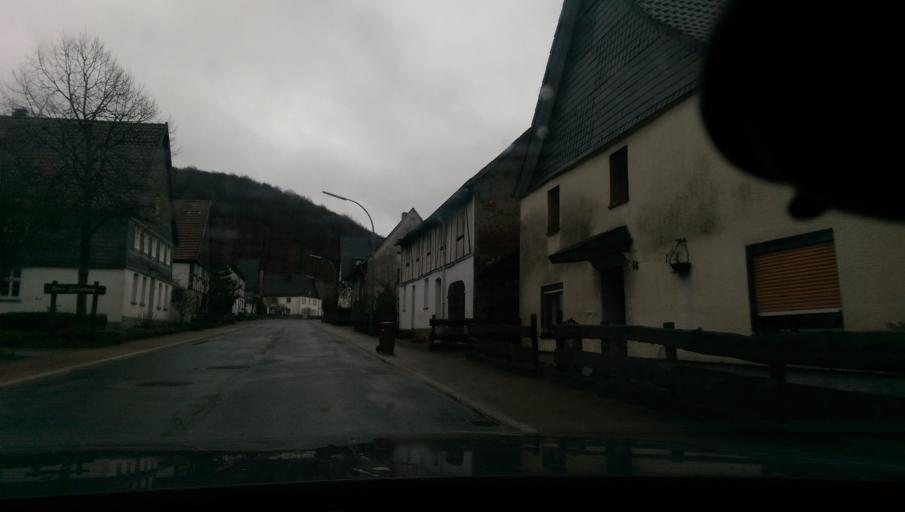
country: DE
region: North Rhine-Westphalia
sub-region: Regierungsbezirk Arnsberg
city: Sundern
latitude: 51.2602
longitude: 7.9625
